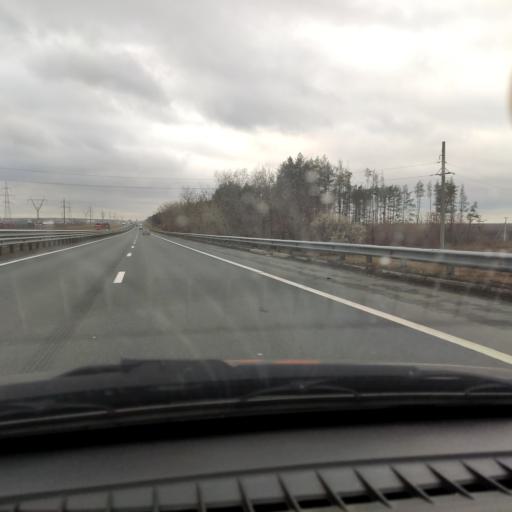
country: RU
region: Samara
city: Povolzhskiy
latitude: 53.5145
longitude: 49.6365
